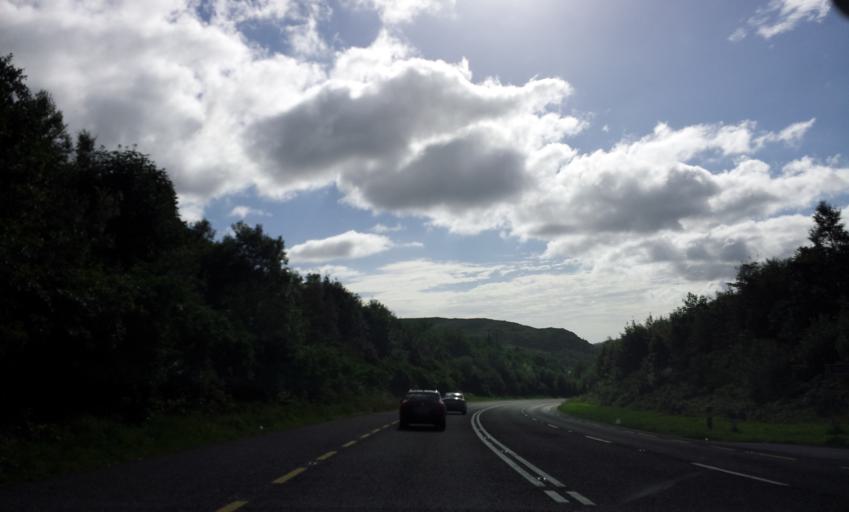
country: IE
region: Munster
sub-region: Ciarrai
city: Cill Airne
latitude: 51.9835
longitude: -9.3021
